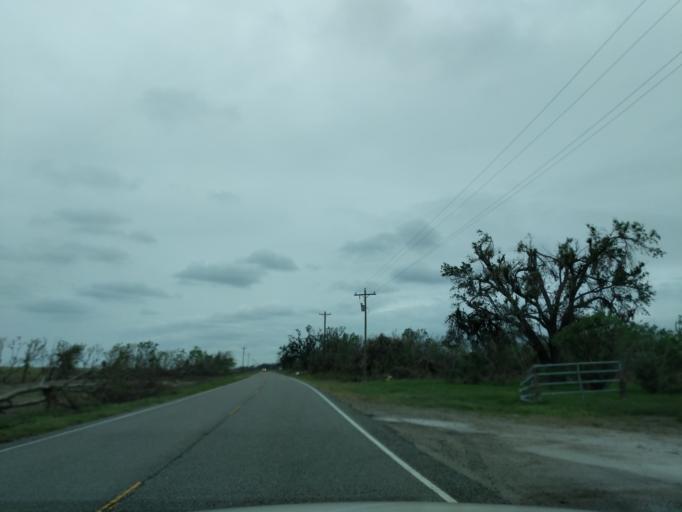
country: US
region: Louisiana
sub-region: Cameron Parish
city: Cameron
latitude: 29.7863
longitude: -93.1761
